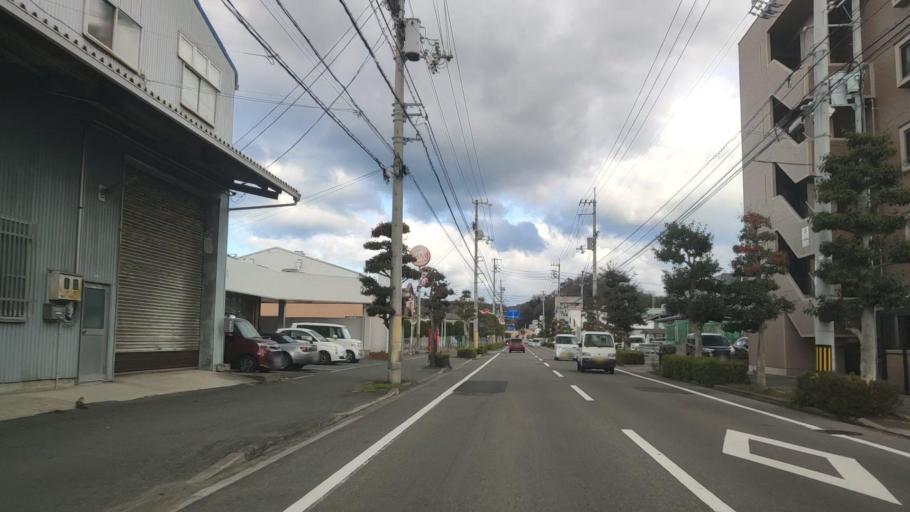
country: JP
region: Ehime
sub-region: Shikoku-chuo Shi
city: Matsuyama
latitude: 33.8649
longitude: 132.7257
